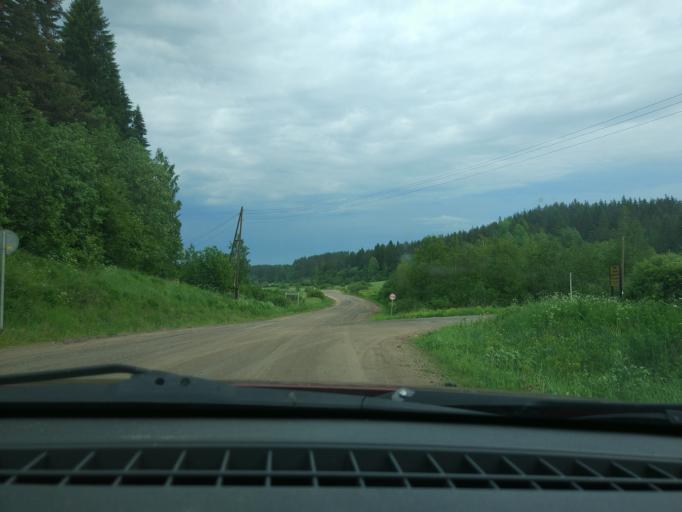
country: RU
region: Leningrad
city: Kuznechnoye
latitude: 61.2742
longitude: 29.8422
